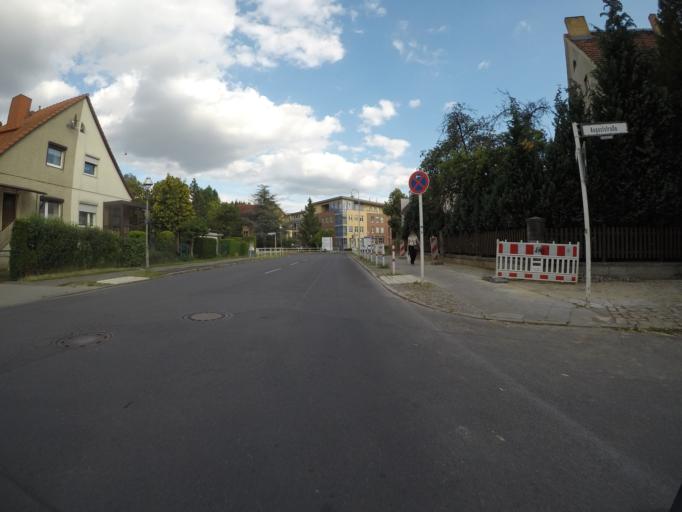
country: DE
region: Berlin
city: Kaulsdorf
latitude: 52.5078
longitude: 13.5914
